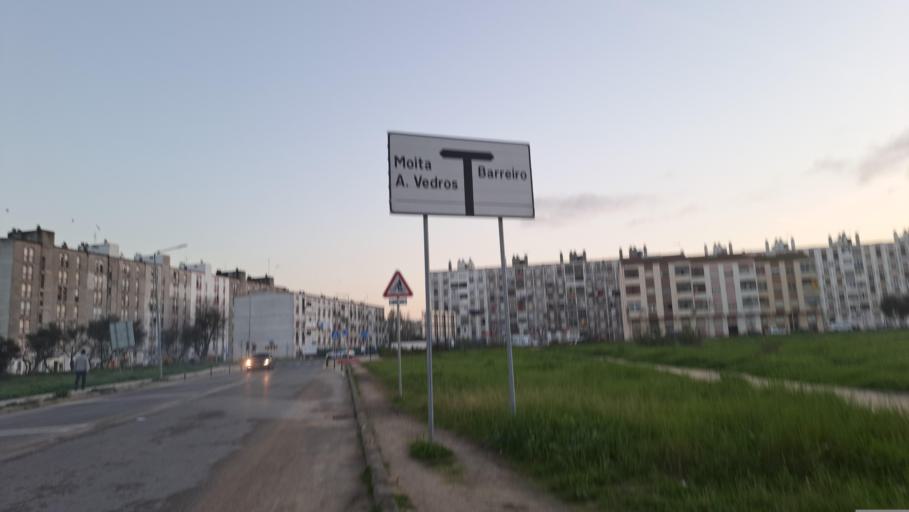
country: PT
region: Setubal
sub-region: Moita
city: Alhos Vedros
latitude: 38.6529
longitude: -9.0374
